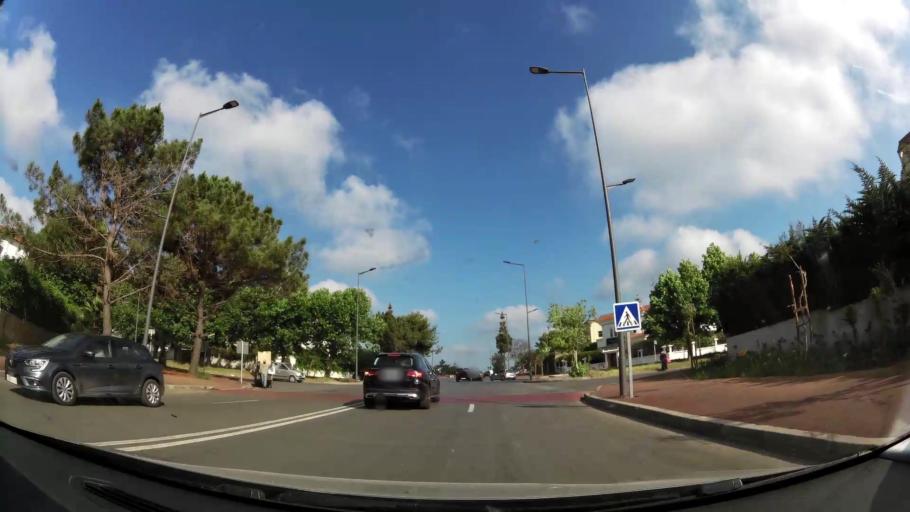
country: MA
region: Rabat-Sale-Zemmour-Zaer
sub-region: Skhirate-Temara
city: Temara
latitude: 33.9582
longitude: -6.8608
